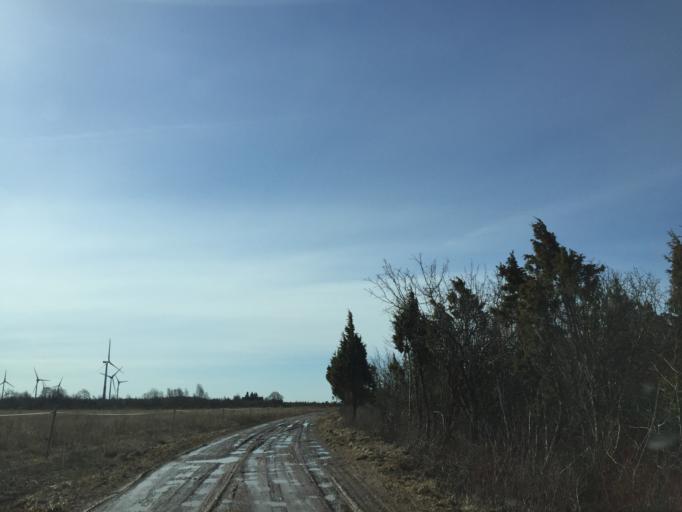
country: EE
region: Laeaene
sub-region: Haapsalu linn
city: Haapsalu
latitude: 58.6515
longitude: 23.5136
